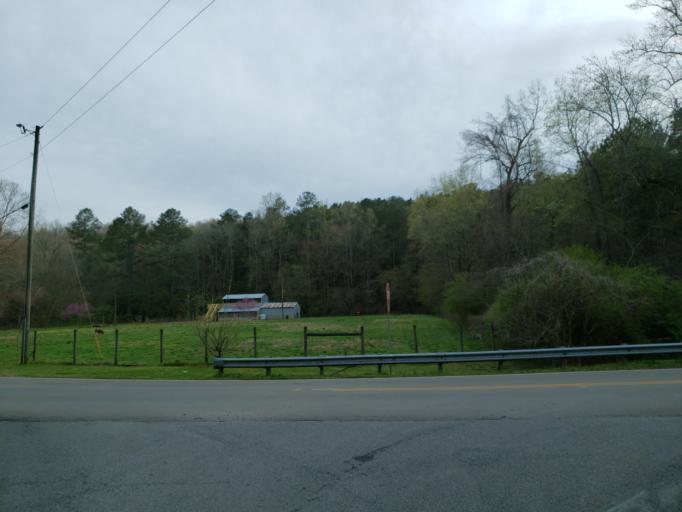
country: US
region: Georgia
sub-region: Pickens County
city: Nelson
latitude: 34.3818
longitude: -84.4274
